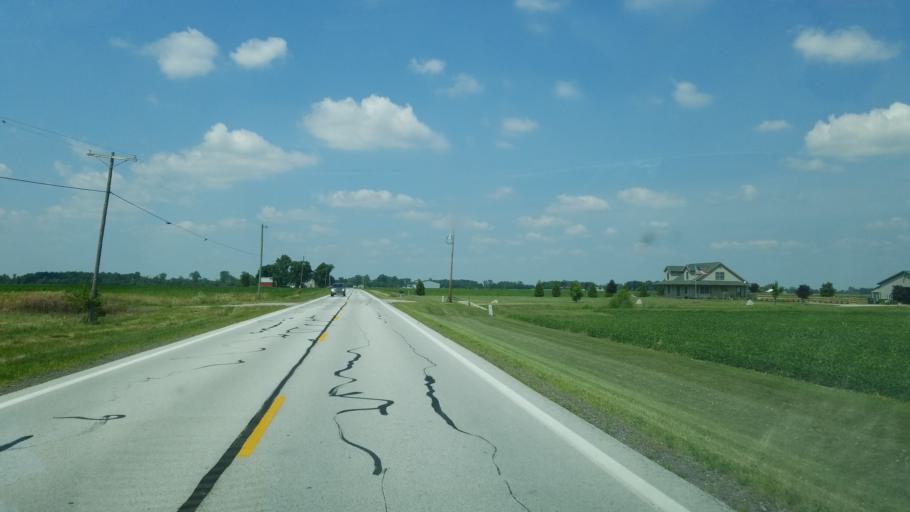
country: US
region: Ohio
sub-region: Henry County
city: Deshler
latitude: 41.2846
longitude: -83.8703
